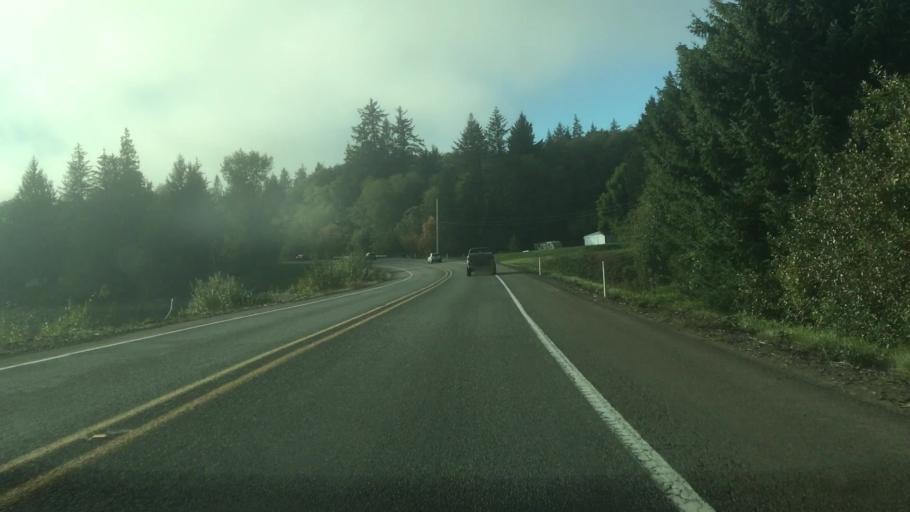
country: US
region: Oregon
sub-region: Clatsop County
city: Astoria
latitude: 46.2700
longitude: -123.8216
